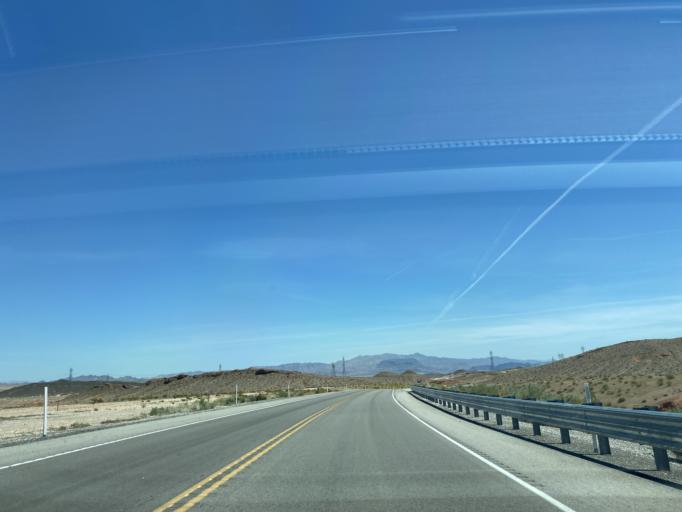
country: US
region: Nevada
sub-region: Clark County
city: Nellis Air Force Base
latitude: 36.1952
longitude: -114.9257
